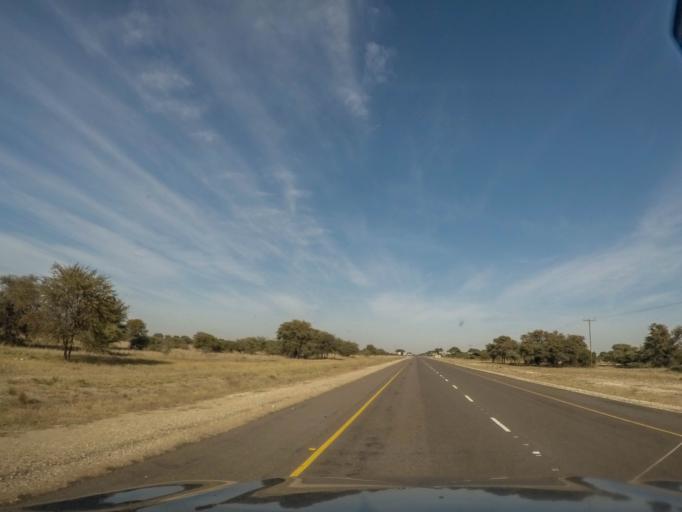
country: BW
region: South East
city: Janeng
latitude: -25.5593
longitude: 25.3101
